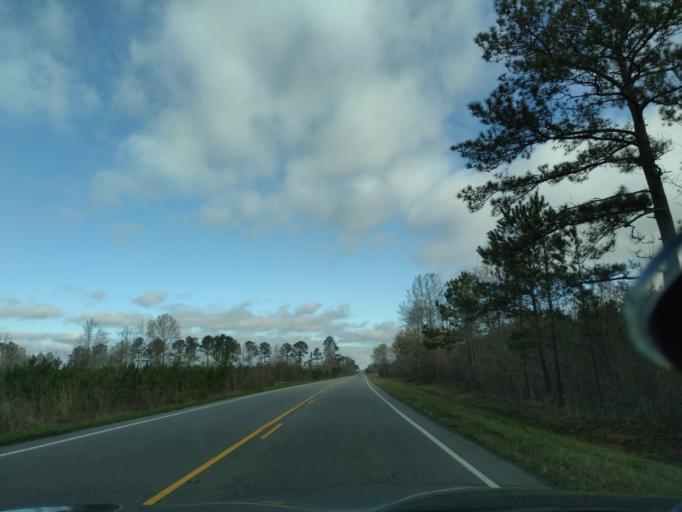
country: US
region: North Carolina
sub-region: Washington County
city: Plymouth
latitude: 35.9914
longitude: -76.7697
